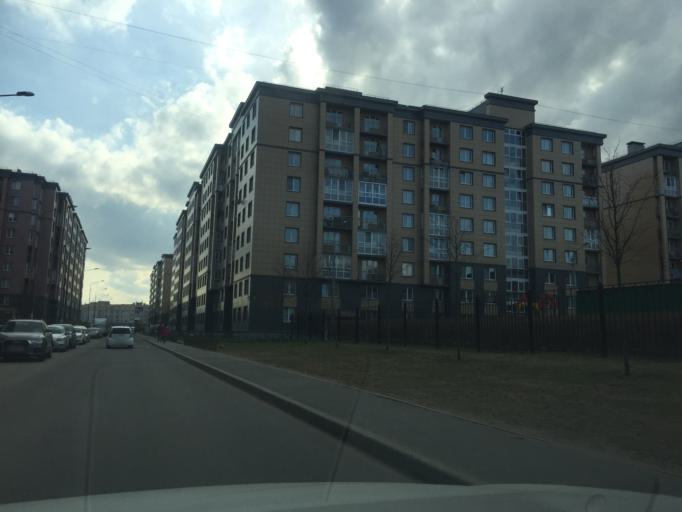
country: RU
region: St.-Petersburg
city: Tyarlevo
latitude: 59.7380
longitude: 30.4733
